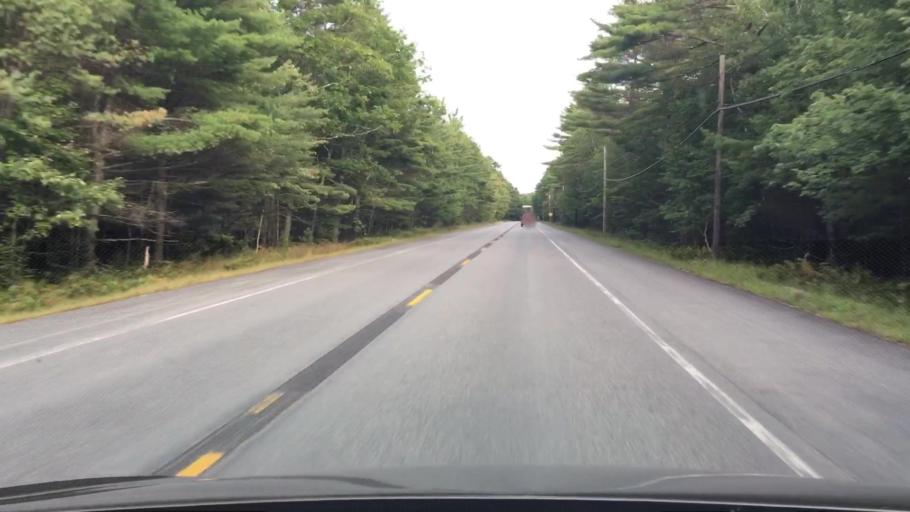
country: US
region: Maine
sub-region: Cumberland County
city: Bridgton
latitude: 44.0645
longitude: -70.7431
